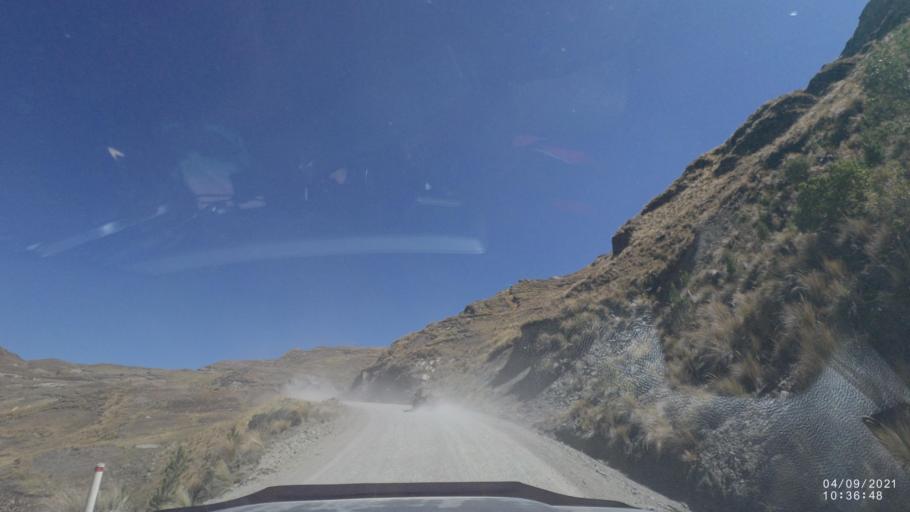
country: BO
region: Cochabamba
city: Sipe Sipe
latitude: -17.2883
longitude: -66.4525
